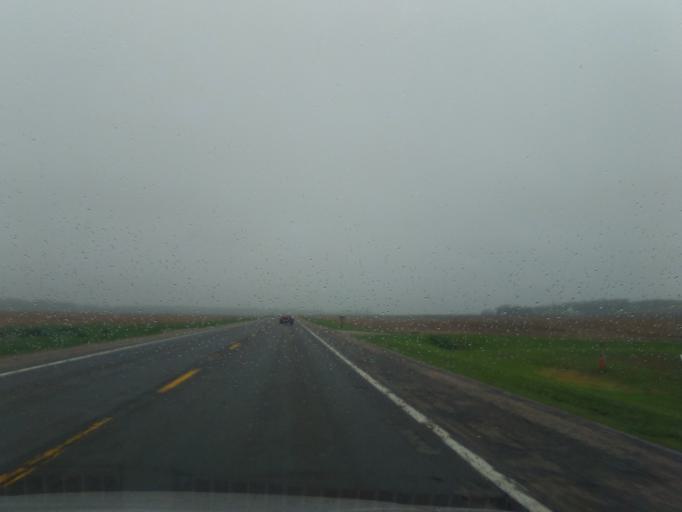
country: US
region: Nebraska
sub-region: Cuming County
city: Wisner
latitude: 41.9567
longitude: -96.8670
